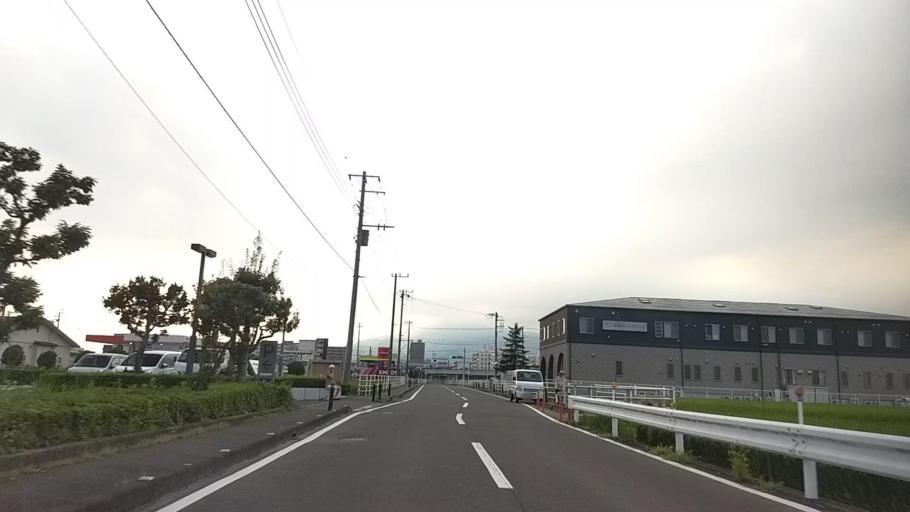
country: JP
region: Kanagawa
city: Atsugi
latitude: 35.4448
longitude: 139.3858
